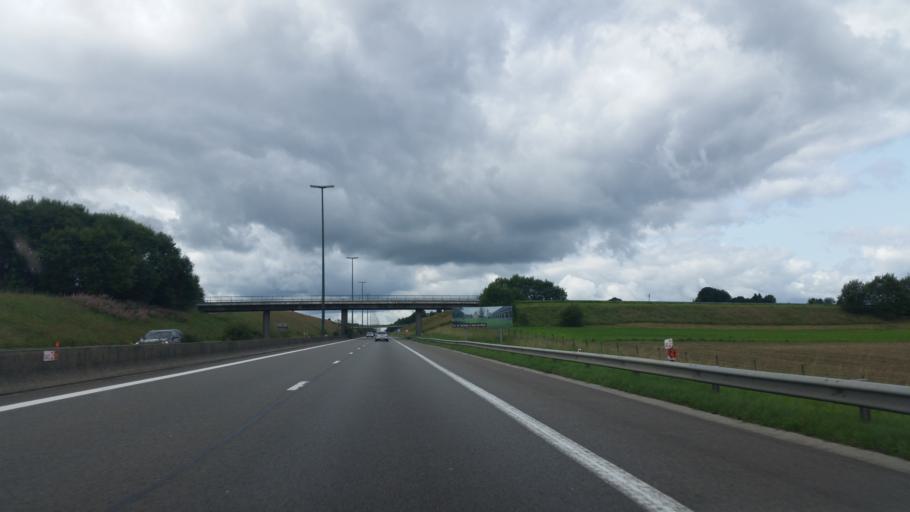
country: BE
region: Wallonia
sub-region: Province du Luxembourg
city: Neufchateau
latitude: 49.8793
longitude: 5.4530
